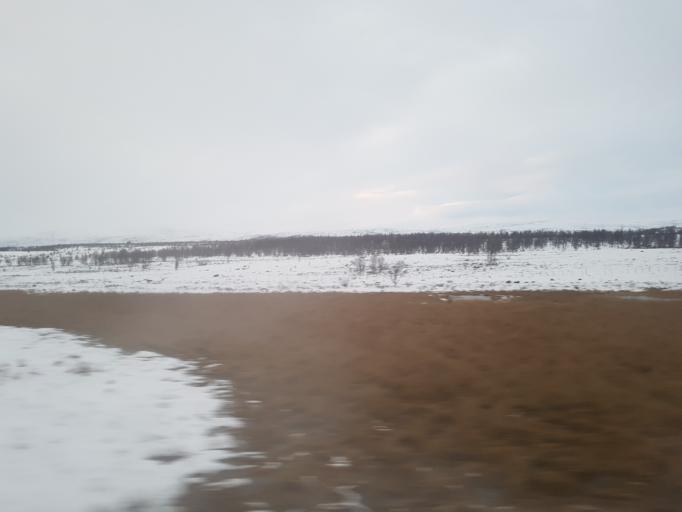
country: NO
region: Oppland
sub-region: Dovre
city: Dovre
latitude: 62.1390
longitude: 9.3199
